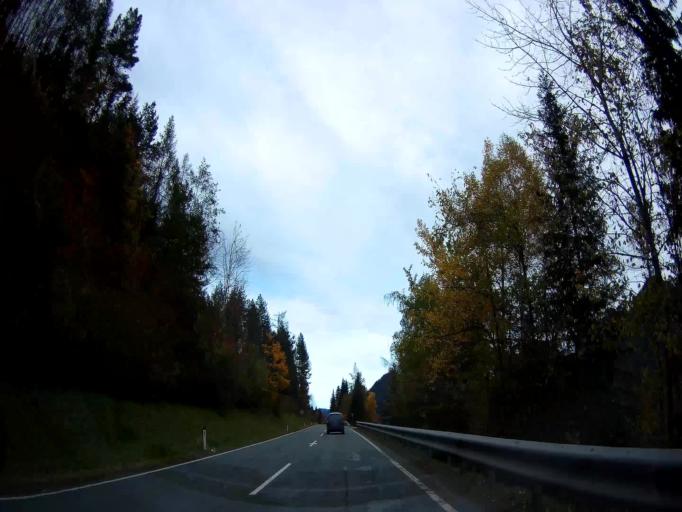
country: AT
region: Salzburg
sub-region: Politischer Bezirk Zell am See
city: Lofer
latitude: 47.5911
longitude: 12.6954
